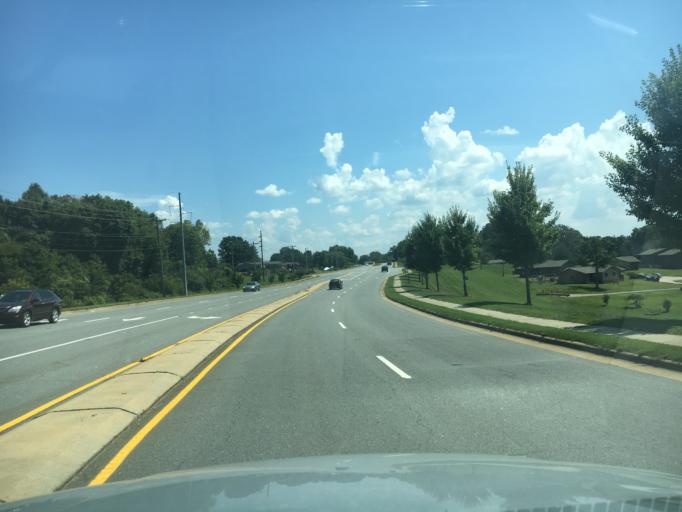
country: US
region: North Carolina
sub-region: Rutherford County
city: Forest City
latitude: 35.3313
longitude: -81.8678
